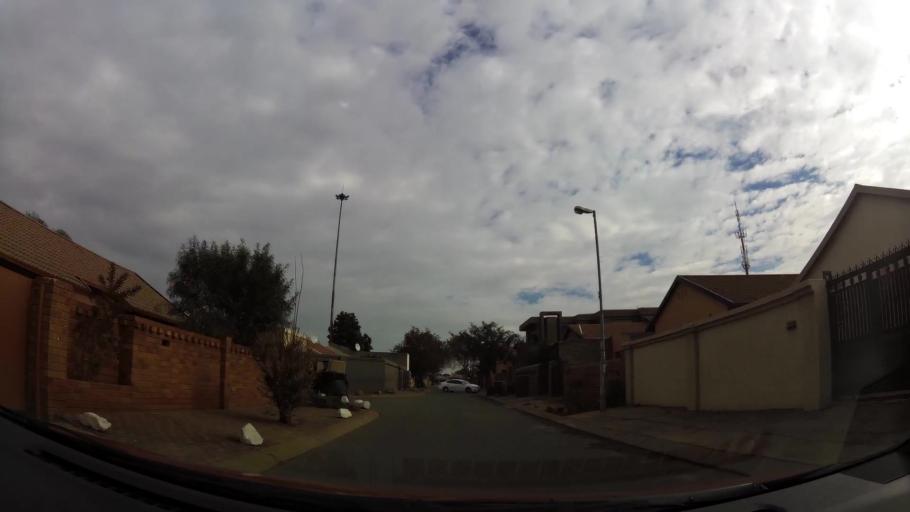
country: ZA
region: Gauteng
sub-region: City of Johannesburg Metropolitan Municipality
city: Soweto
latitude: -26.2765
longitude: 27.8361
